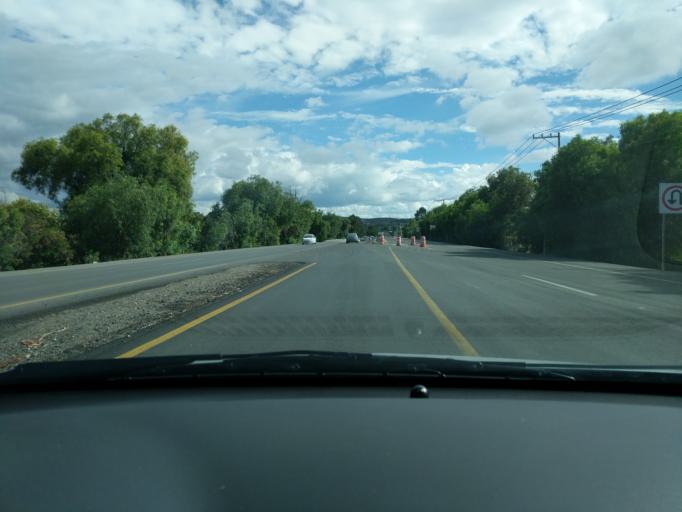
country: MX
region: Queretaro
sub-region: El Marques
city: La Loma
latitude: 20.5868
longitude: -100.2499
